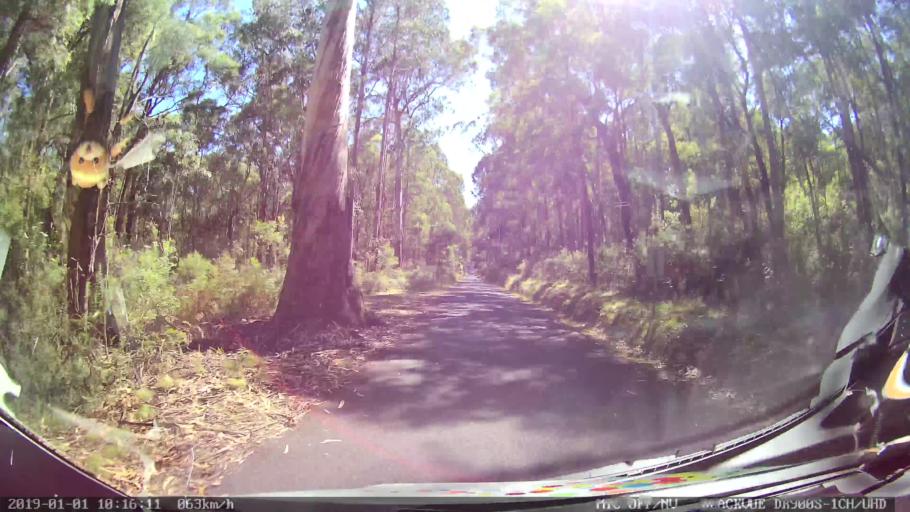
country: AU
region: New South Wales
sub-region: Snowy River
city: Jindabyne
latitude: -36.0955
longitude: 148.1652
